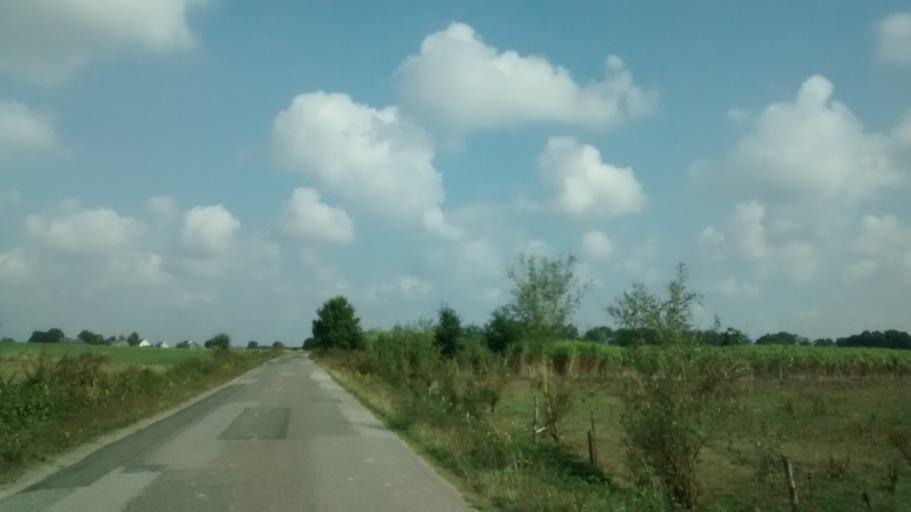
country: FR
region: Brittany
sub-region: Departement d'Ille-et-Vilaine
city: Erbree
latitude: 48.1286
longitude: -1.1023
